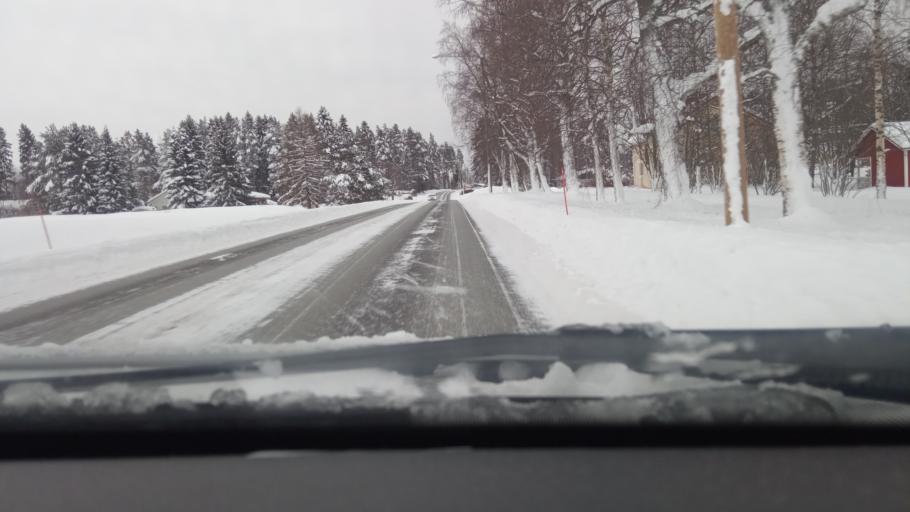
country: FI
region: Southern Ostrobothnia
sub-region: Jaerviseutu
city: Alajaervi
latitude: 62.9898
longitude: 23.8455
